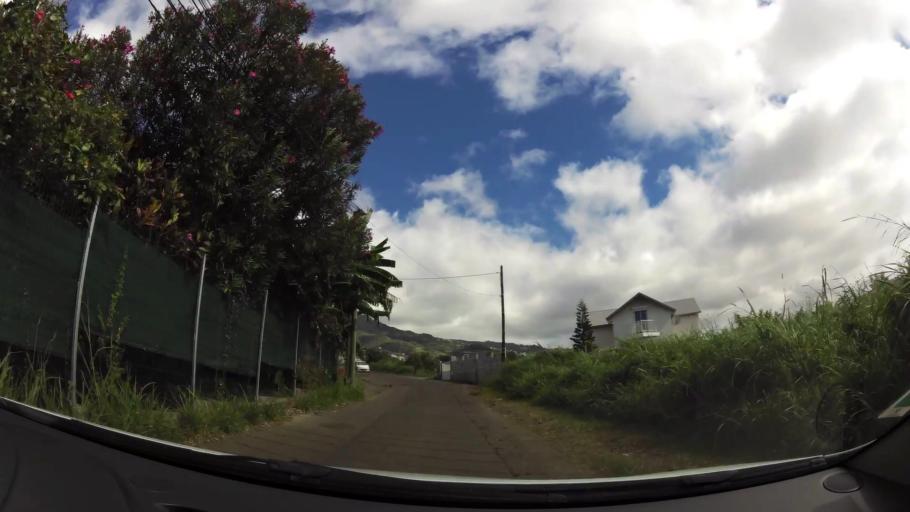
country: RE
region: Reunion
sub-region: Reunion
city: Sainte-Marie
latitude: -20.9246
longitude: 55.4996
